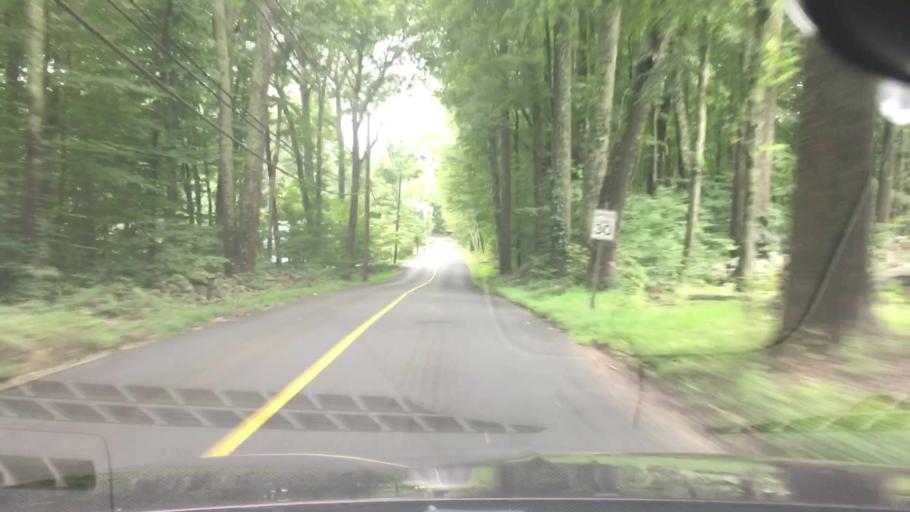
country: US
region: Connecticut
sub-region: New Haven County
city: Madison
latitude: 41.3381
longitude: -72.5783
